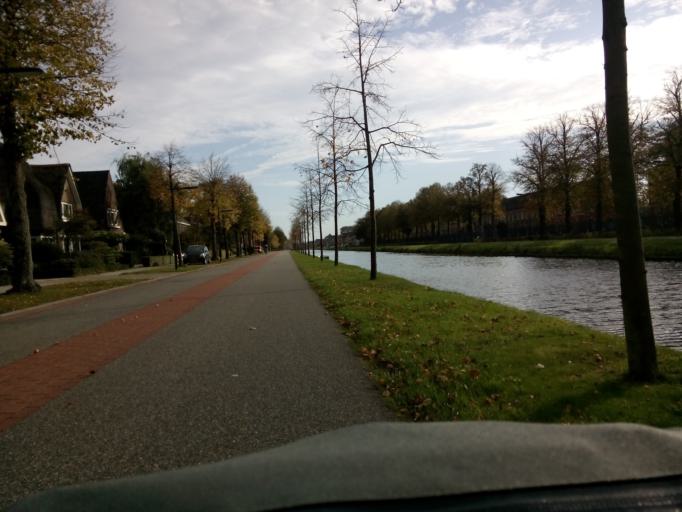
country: NL
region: Drenthe
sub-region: Gemeente Assen
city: Assen
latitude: 52.9944
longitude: 6.5414
